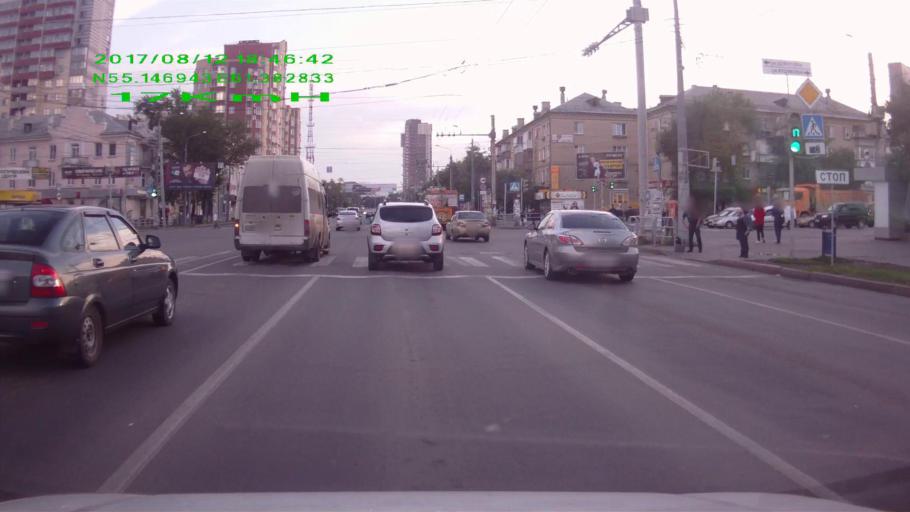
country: RU
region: Chelyabinsk
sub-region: Gorod Chelyabinsk
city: Chelyabinsk
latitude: 55.1430
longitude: 61.3771
